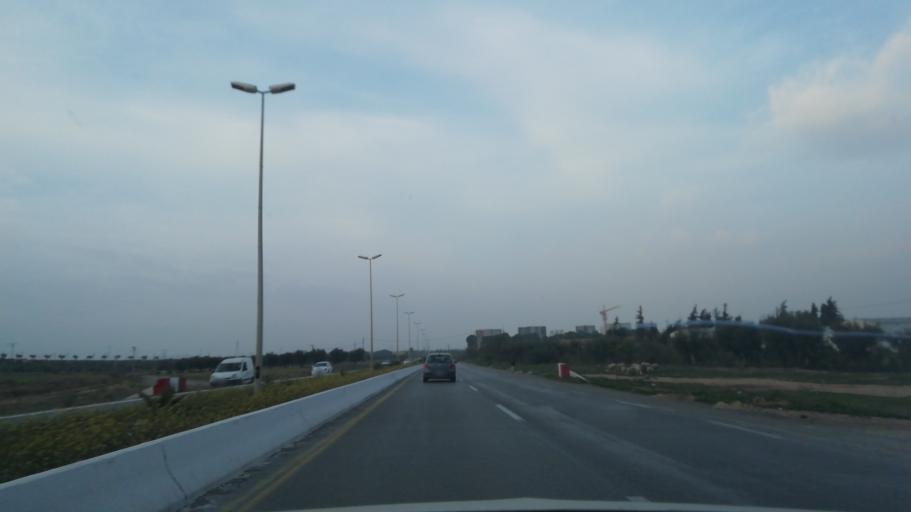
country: DZ
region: Sidi Bel Abbes
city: Sidi Bel Abbes
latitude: 35.1991
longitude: -0.6608
